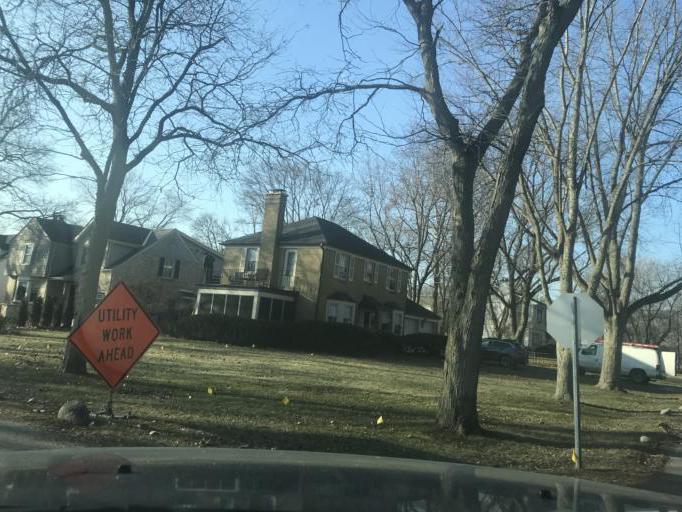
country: US
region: Illinois
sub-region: Cook County
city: Northfield
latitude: 42.0995
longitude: -87.7624
